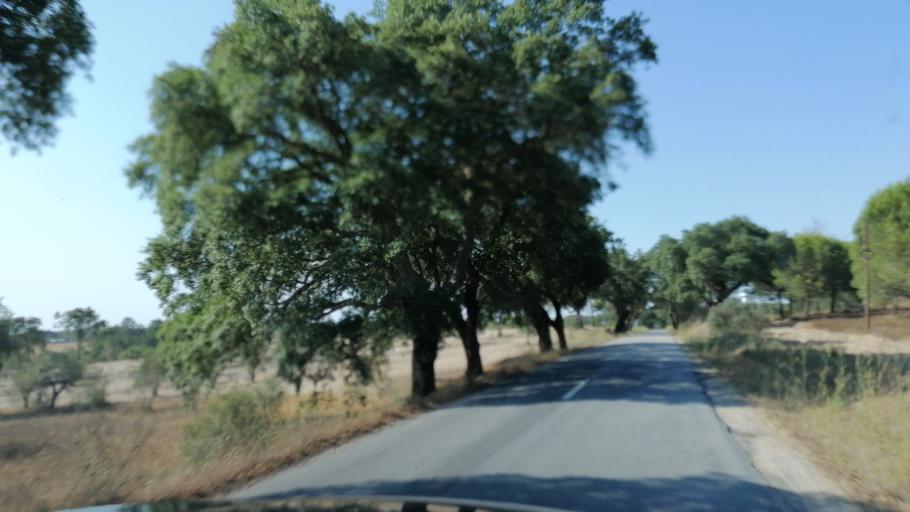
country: PT
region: Santarem
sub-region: Benavente
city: Poceirao
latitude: 38.7542
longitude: -8.6320
